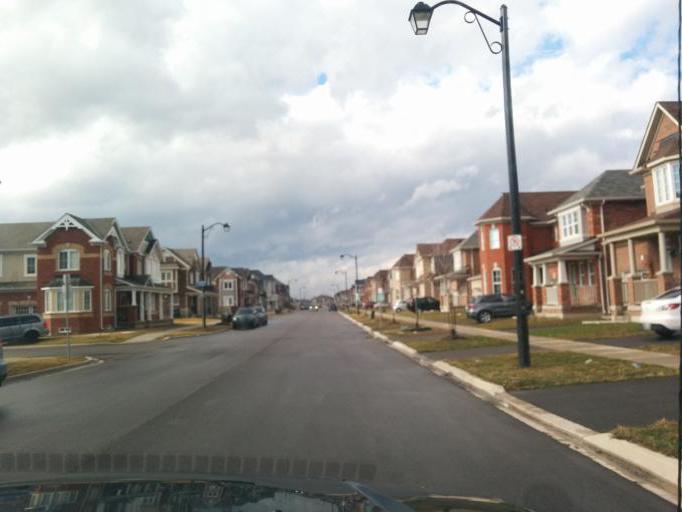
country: CA
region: Ontario
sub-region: Halton
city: Milton
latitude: 43.4883
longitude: -79.8636
